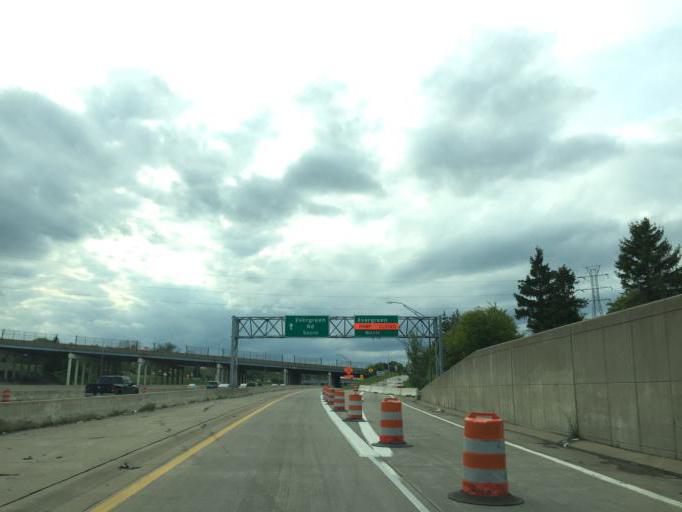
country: US
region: Michigan
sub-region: Wayne County
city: Dearborn Heights
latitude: 42.3793
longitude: -83.2342
